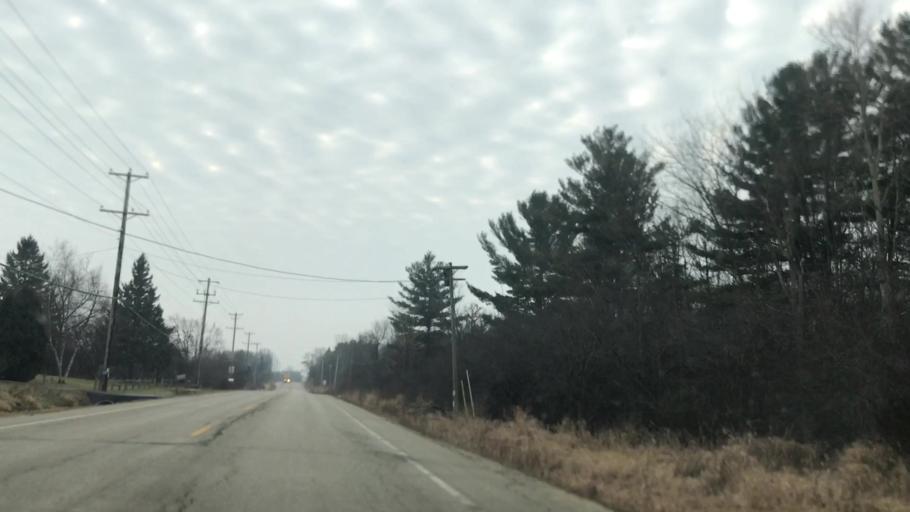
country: US
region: Wisconsin
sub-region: Ozaukee County
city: Cedarburg
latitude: 43.2858
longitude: -88.0041
